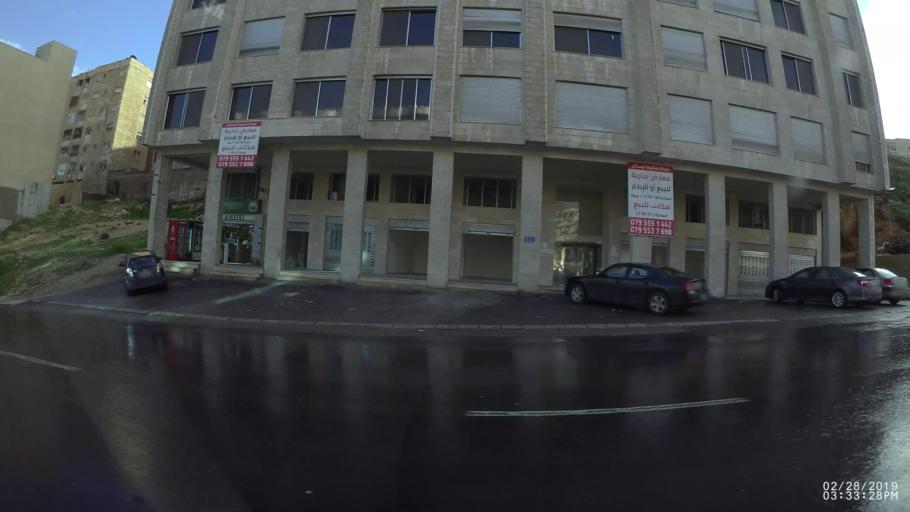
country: JO
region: Amman
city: Al Jubayhah
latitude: 31.9968
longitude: 35.8833
